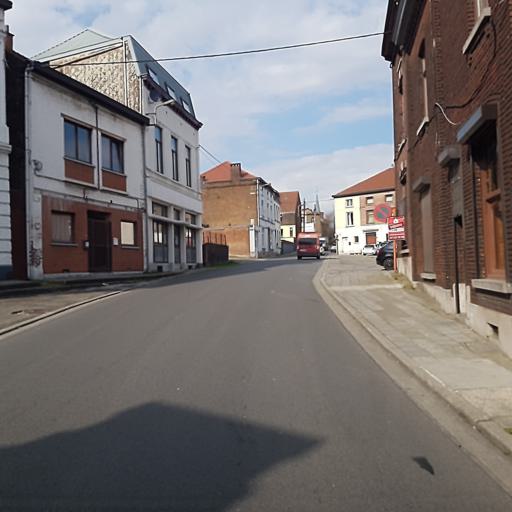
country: BE
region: Wallonia
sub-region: Province du Hainaut
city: Charleroi
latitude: 50.4285
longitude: 4.4479
